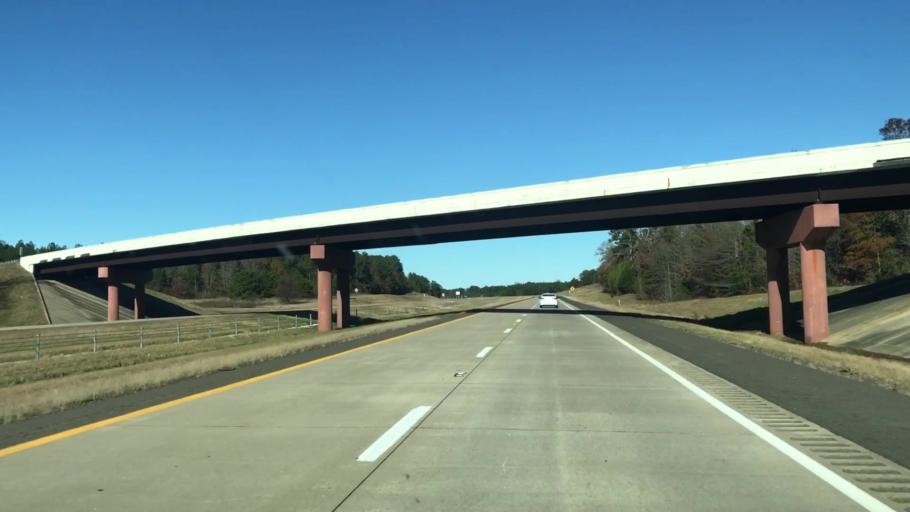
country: US
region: Texas
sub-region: Bowie County
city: Texarkana
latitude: 33.3313
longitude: -93.9596
